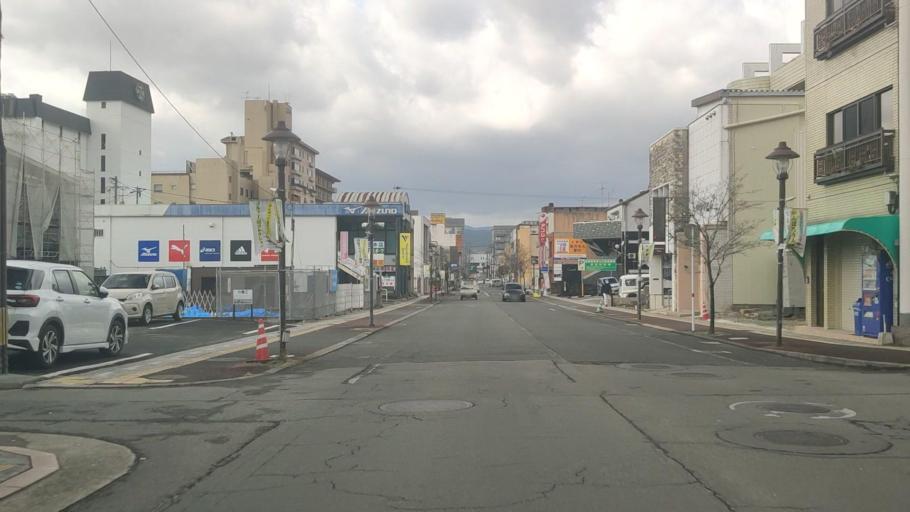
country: JP
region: Kumamoto
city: Hitoyoshi
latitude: 32.2141
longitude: 130.7621
